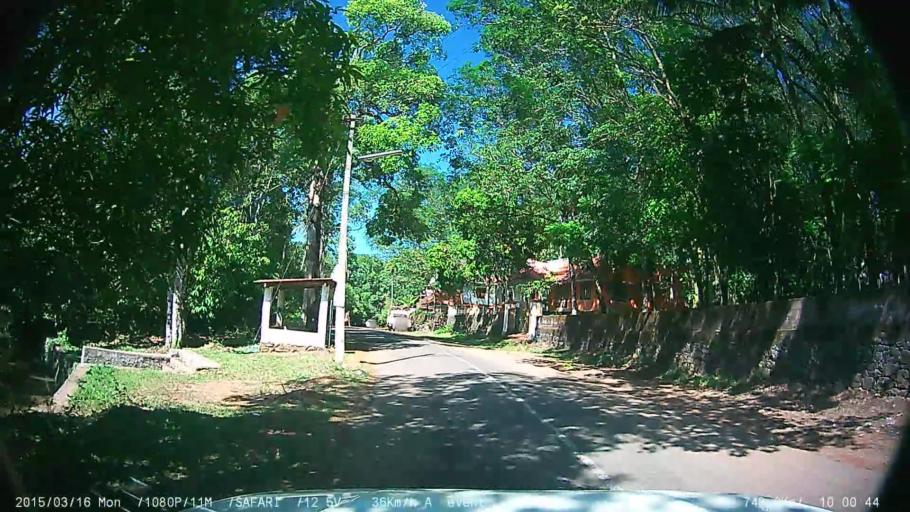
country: IN
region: Kerala
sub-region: Kottayam
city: Palackattumala
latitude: 9.7821
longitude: 76.5879
